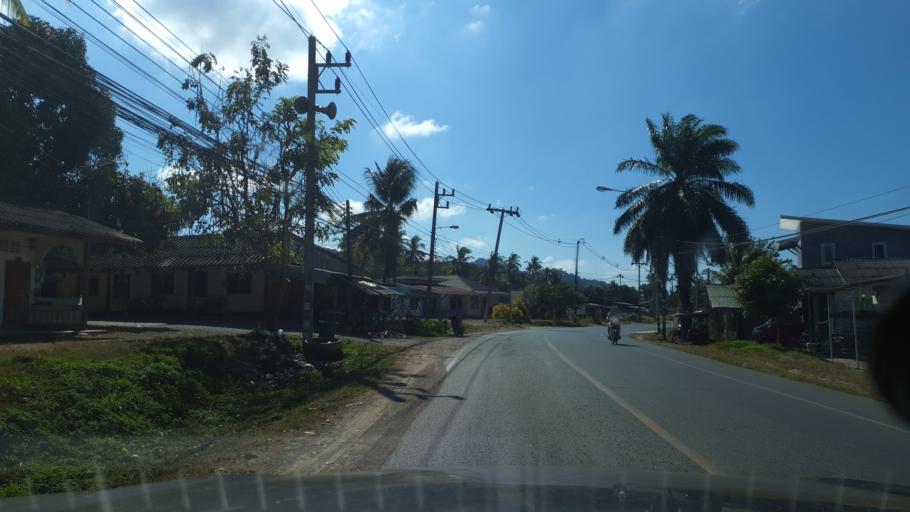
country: TH
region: Phangnga
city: Ban Ao Nang
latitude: 8.0589
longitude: 98.8142
